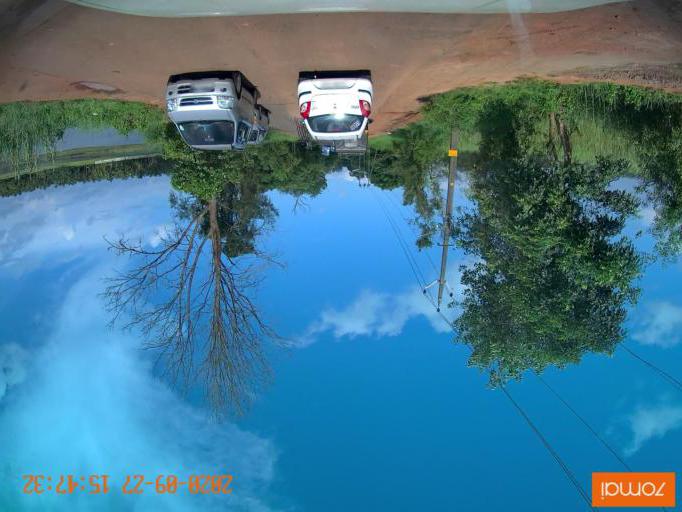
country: IN
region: Kerala
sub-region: Thrissur District
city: Thanniyam
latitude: 10.4821
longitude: 76.1294
